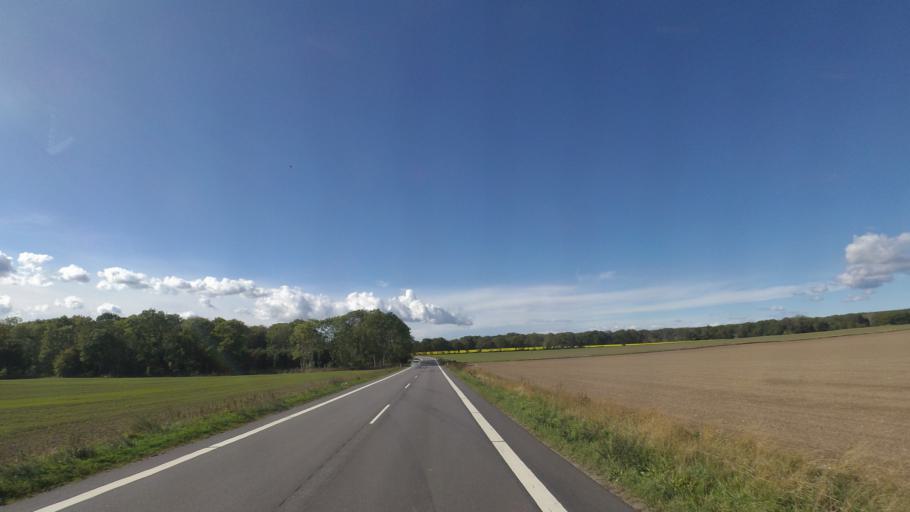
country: DK
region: Capital Region
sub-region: Bornholm Kommune
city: Akirkeby
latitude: 55.0687
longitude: 14.9869
